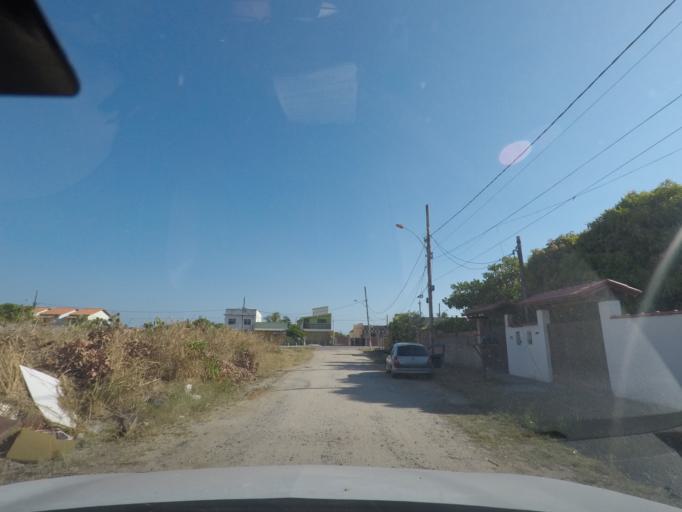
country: BR
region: Rio de Janeiro
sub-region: Marica
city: Marica
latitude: -22.9695
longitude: -42.9127
